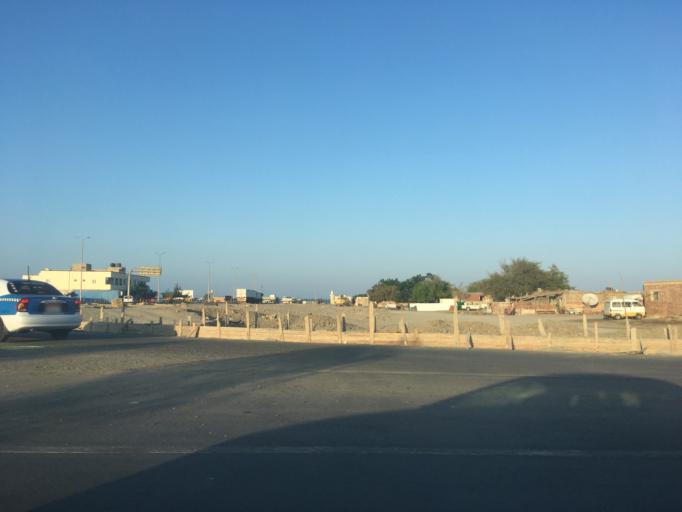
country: EG
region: Red Sea
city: Marsa Alam
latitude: 25.0691
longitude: 34.8907
